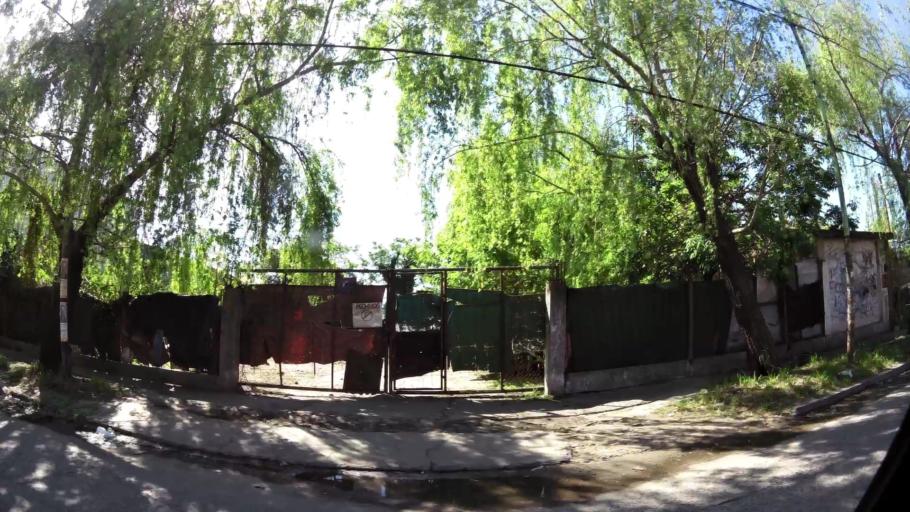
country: AR
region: Buenos Aires
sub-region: Partido de Quilmes
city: Quilmes
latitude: -34.7943
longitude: -58.2489
